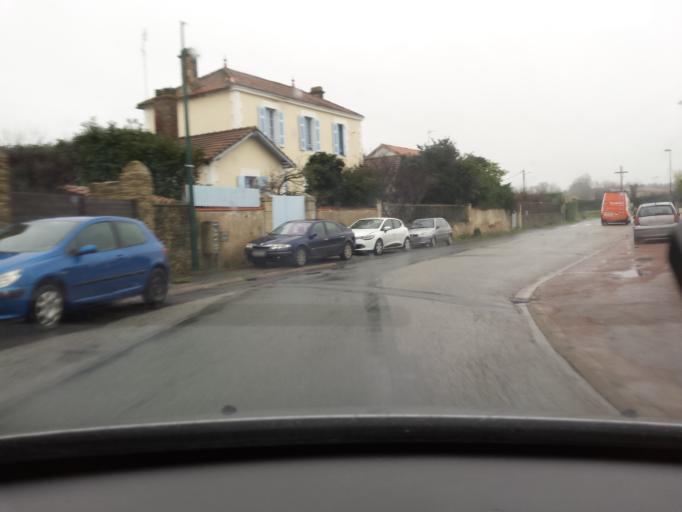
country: FR
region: Pays de la Loire
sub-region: Departement de la Vendee
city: Mareuil-sur-Lay-Dissais
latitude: 46.5539
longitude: -1.1578
